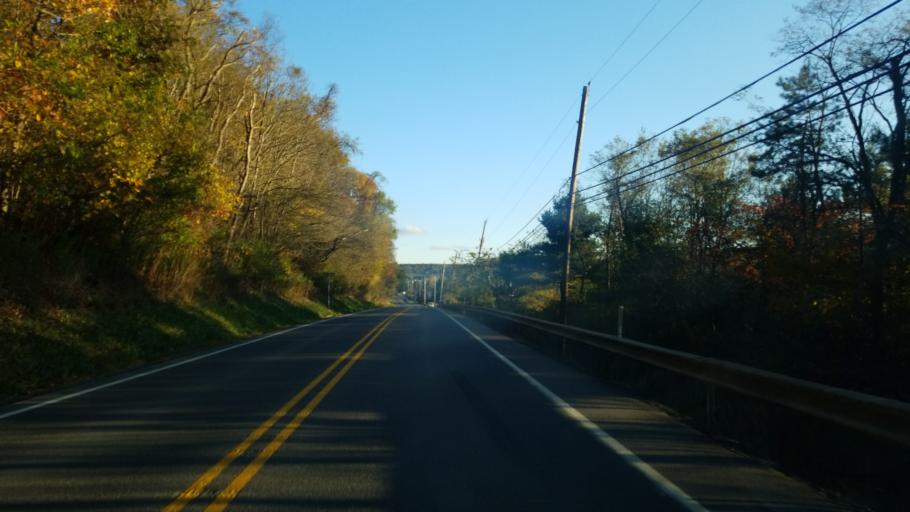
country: US
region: Pennsylvania
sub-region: Jefferson County
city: Punxsutawney
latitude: 40.9616
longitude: -78.9673
